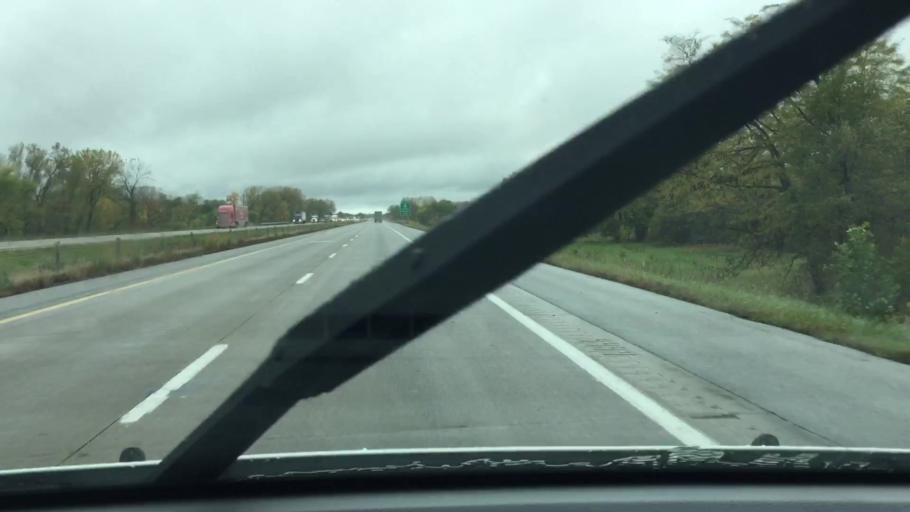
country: US
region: Iowa
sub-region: Jasper County
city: Colfax
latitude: 41.6980
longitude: -93.2198
